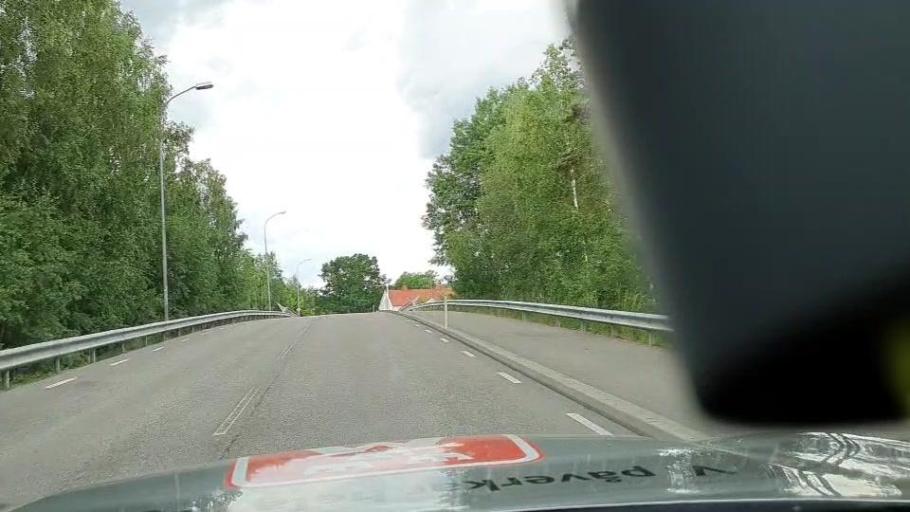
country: SE
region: Kalmar
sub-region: Emmaboda Kommun
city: Emmaboda
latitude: 56.5342
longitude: 15.5868
